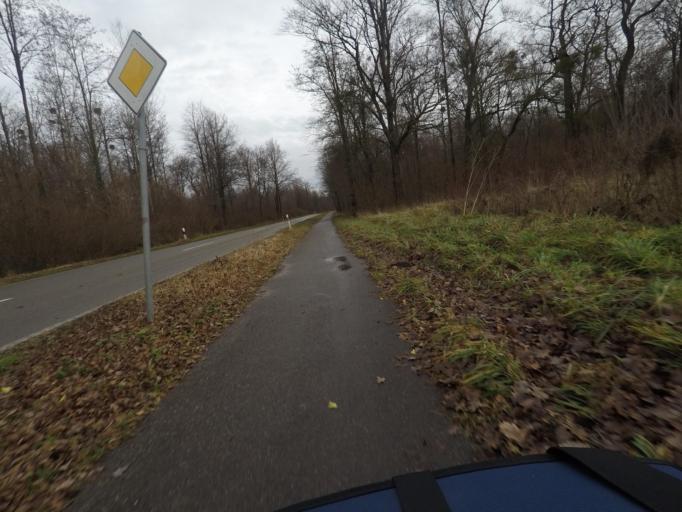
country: DE
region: Baden-Wuerttemberg
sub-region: Karlsruhe Region
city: Au am Rhein
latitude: 48.9633
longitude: 8.2504
